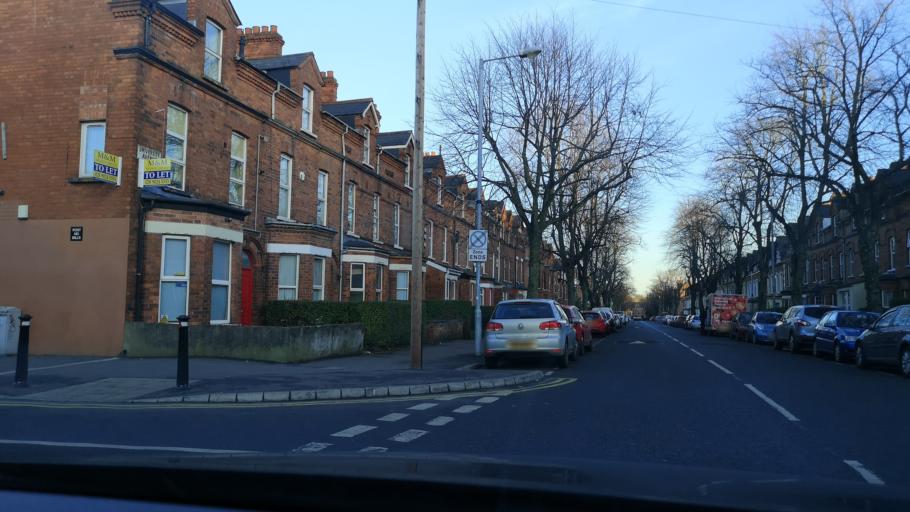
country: GB
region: Northern Ireland
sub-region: City of Belfast
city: Belfast
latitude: 54.5848
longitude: -5.9287
